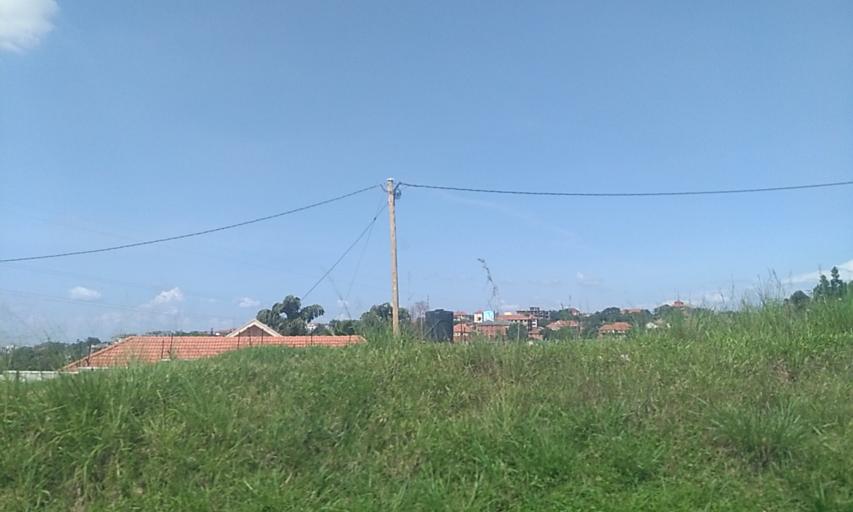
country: UG
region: Central Region
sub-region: Wakiso District
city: Kireka
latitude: 0.3619
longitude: 32.6347
